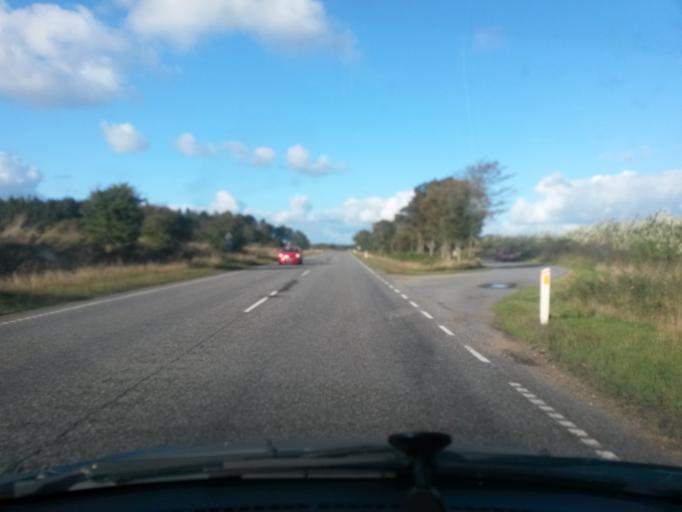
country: DK
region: Central Jutland
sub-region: Silkeborg Kommune
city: Kjellerup
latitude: 56.3155
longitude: 9.3294
